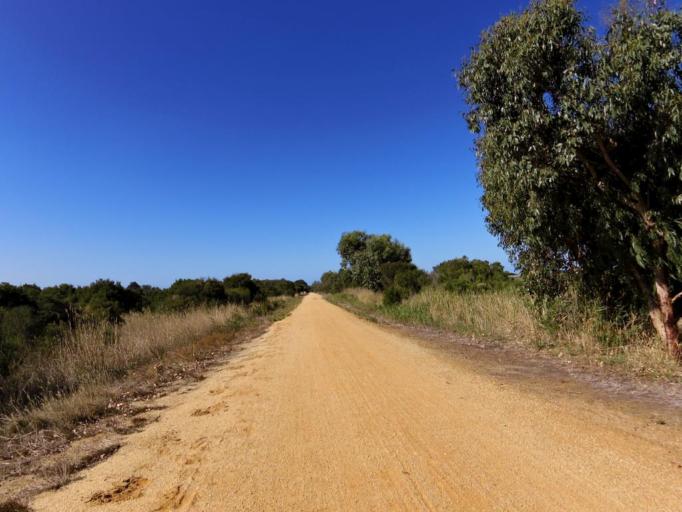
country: AU
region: Victoria
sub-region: Bass Coast
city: North Wonthaggi
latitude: -38.5825
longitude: 145.5539
